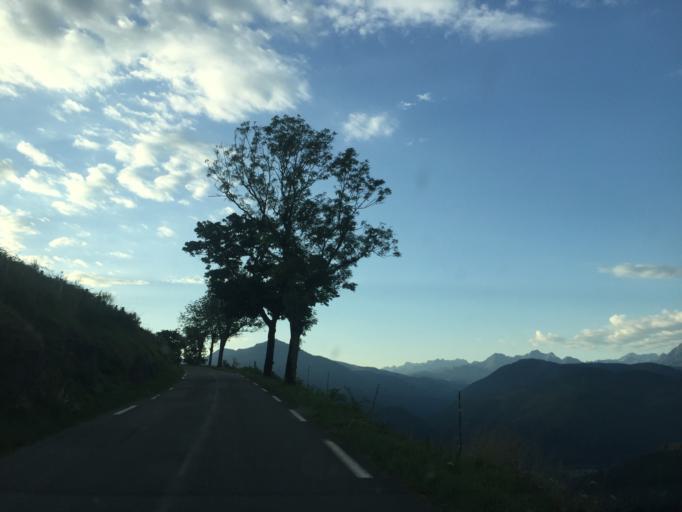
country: FR
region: Midi-Pyrenees
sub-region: Departement des Hautes-Pyrenees
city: Saint-Lary-Soulan
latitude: 42.9268
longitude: 0.3490
